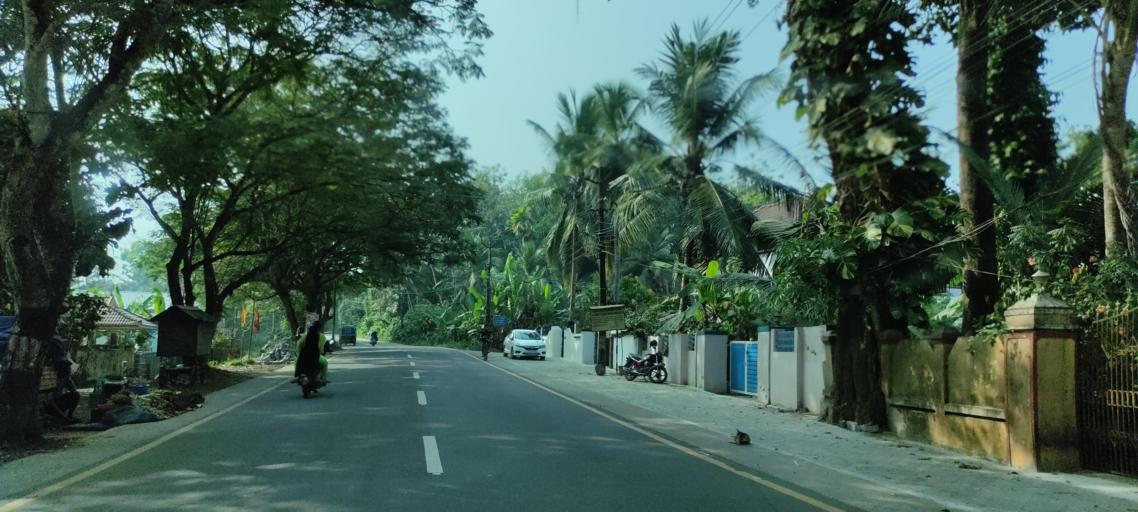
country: IN
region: Kerala
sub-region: Pattanamtitta
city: Tiruvalla
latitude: 9.3692
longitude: 76.5399
